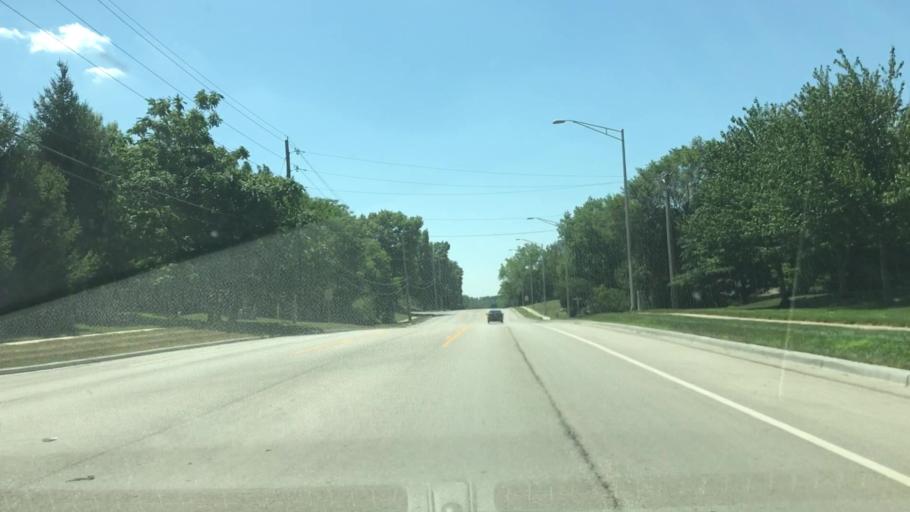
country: US
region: Missouri
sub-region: Jackson County
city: Lees Summit
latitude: 38.9269
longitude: -94.4249
